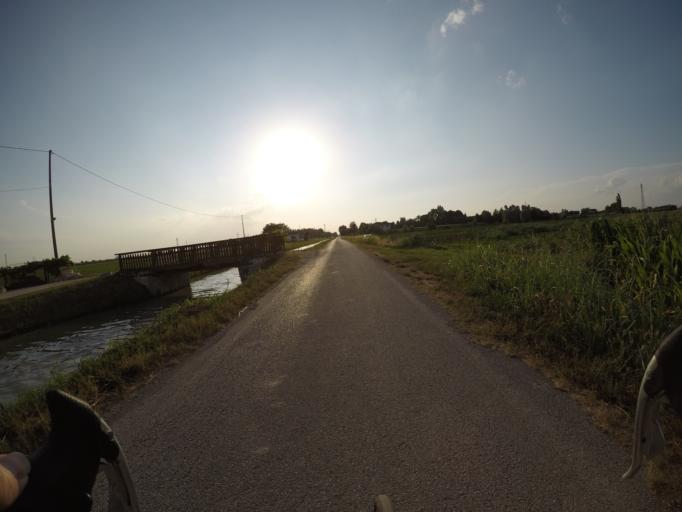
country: IT
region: Veneto
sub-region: Provincia di Rovigo
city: San Bellino
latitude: 45.0440
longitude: 11.5898
